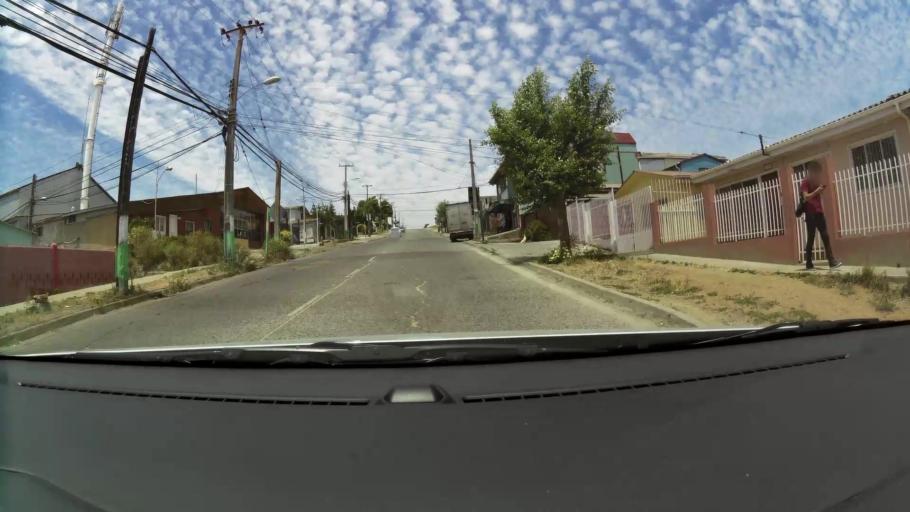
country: CL
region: Valparaiso
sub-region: Provincia de Valparaiso
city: Vina del Mar
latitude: -33.0497
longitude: -71.5753
